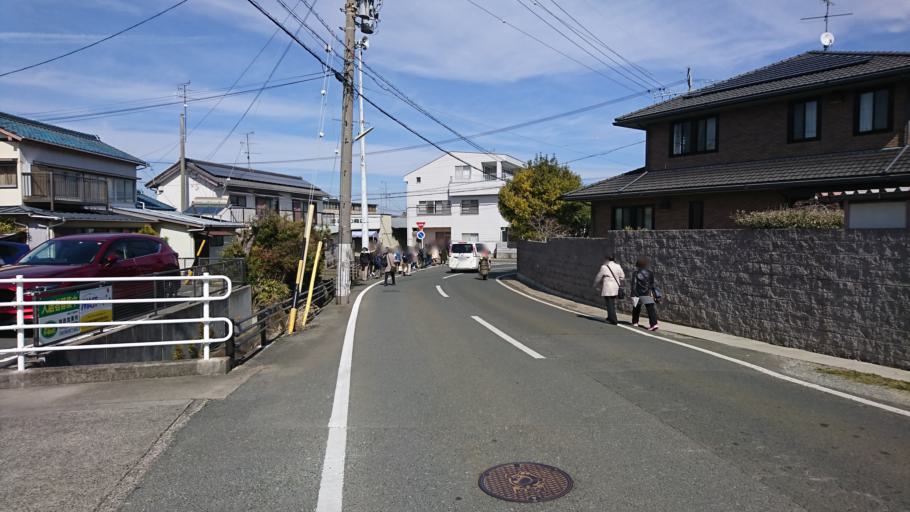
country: JP
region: Shizuoka
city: Kosai-shi
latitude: 34.7203
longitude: 137.5396
